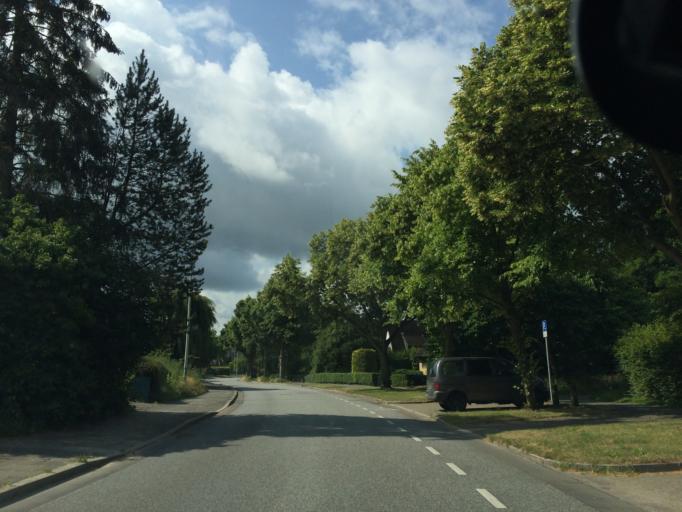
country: DE
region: Schleswig-Holstein
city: Kronshagen
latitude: 54.3226
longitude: 10.0664
